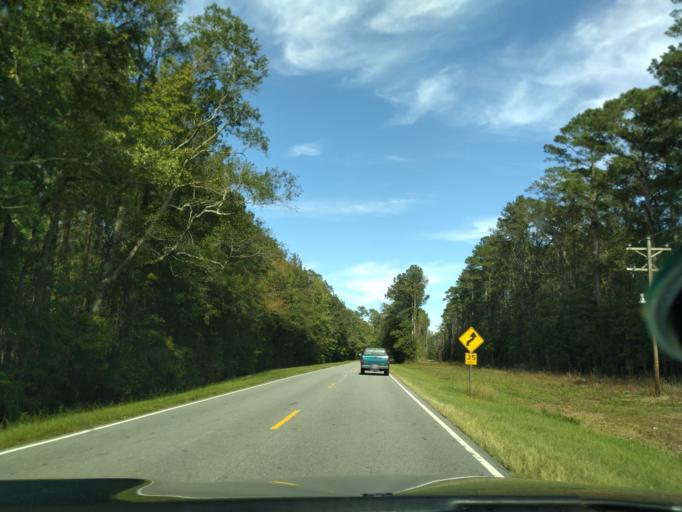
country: US
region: North Carolina
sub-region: Beaufort County
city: Belhaven
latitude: 35.6307
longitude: -76.6170
